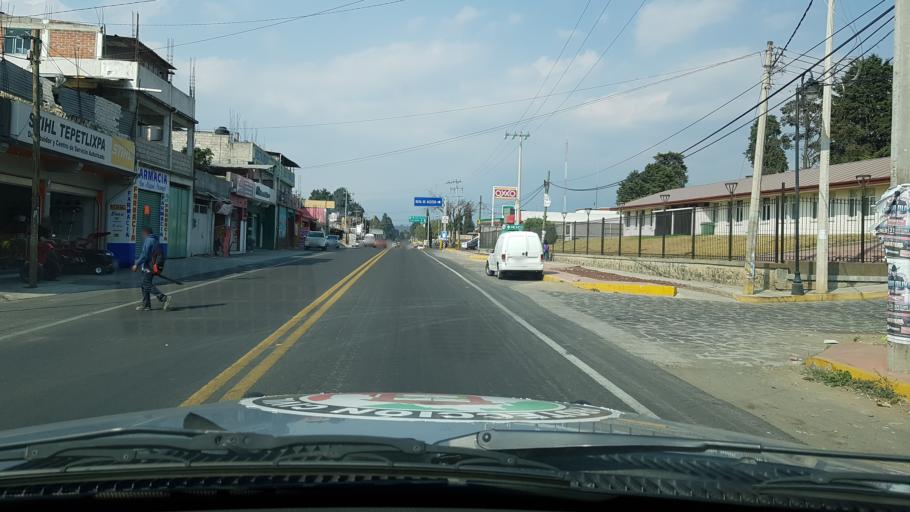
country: MX
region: Mexico
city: Tepetlixpa
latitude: 19.0304
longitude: -98.8134
